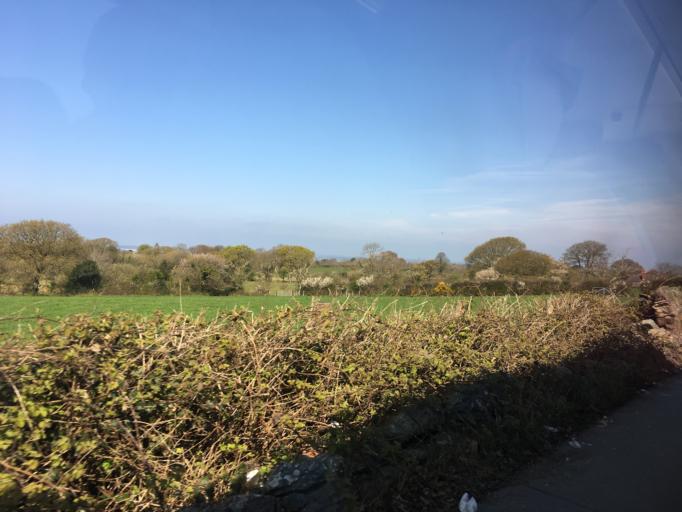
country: GB
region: Wales
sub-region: Gwynedd
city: Llanwnda
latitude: 53.0858
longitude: -4.2787
